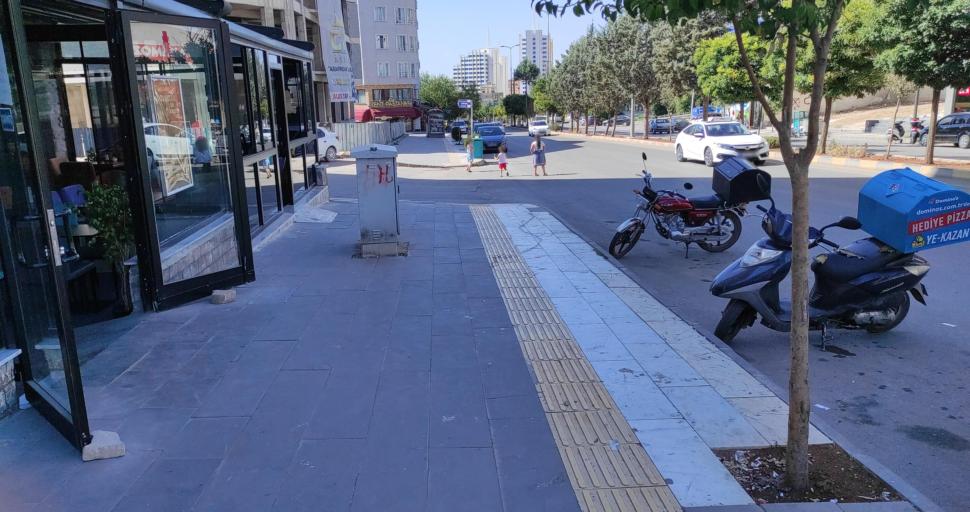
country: TR
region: Kilis
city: Kilis
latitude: 36.7276
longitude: 37.1006
